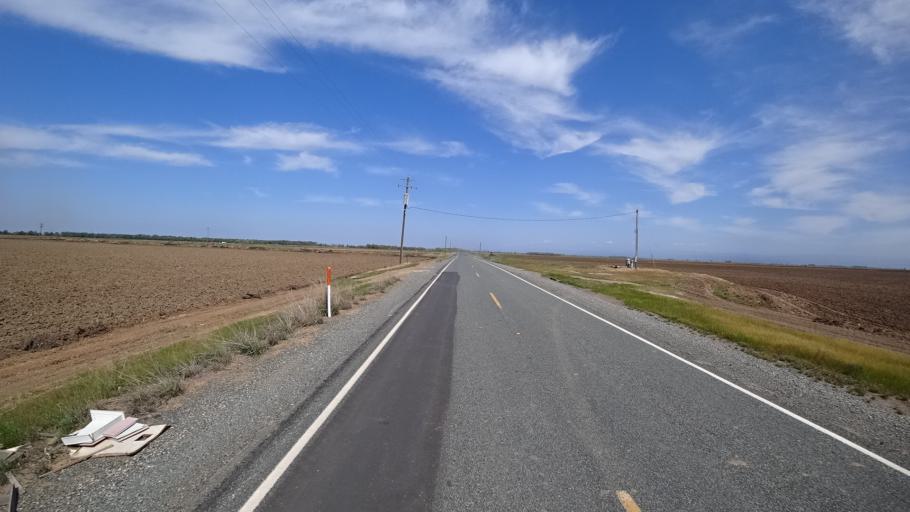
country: US
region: California
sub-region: Butte County
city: Durham
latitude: 39.5025
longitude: -121.8574
